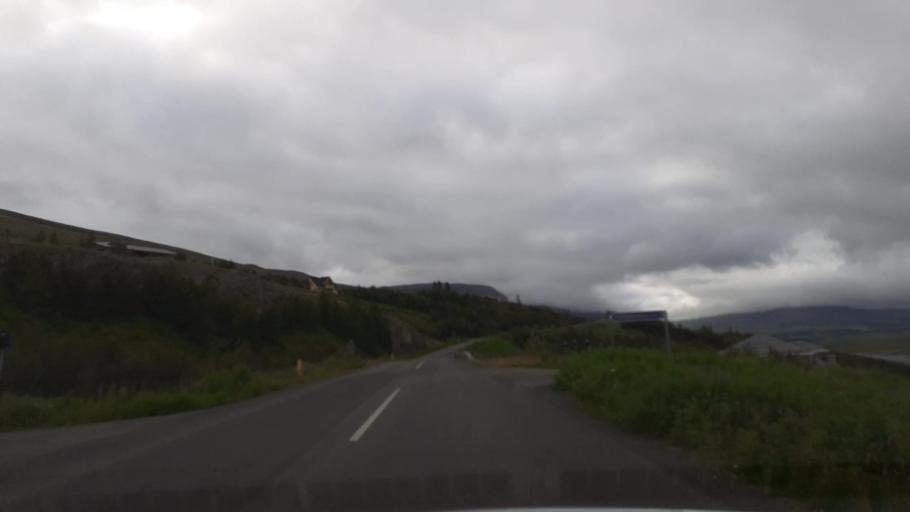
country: IS
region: Northeast
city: Akureyri
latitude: 65.6845
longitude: -18.0455
